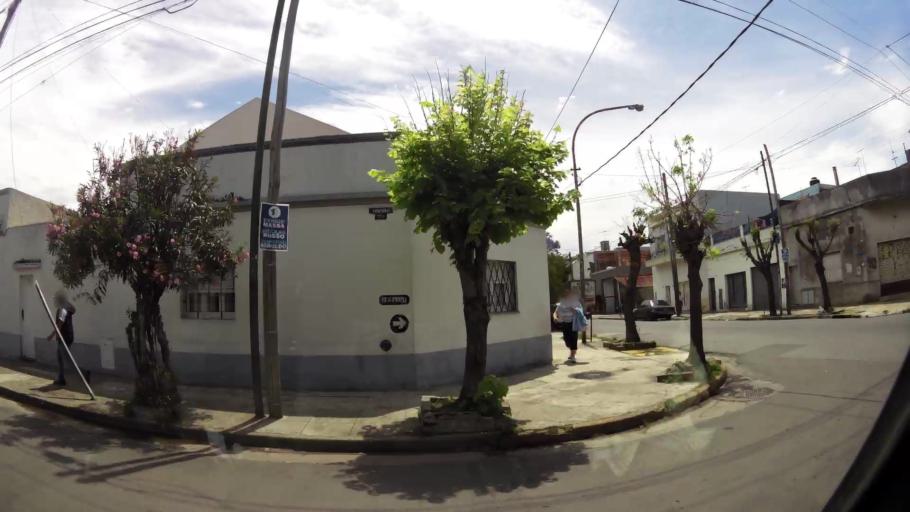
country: AR
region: Buenos Aires
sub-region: Partido de Lanus
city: Lanus
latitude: -34.6694
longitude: -58.4055
